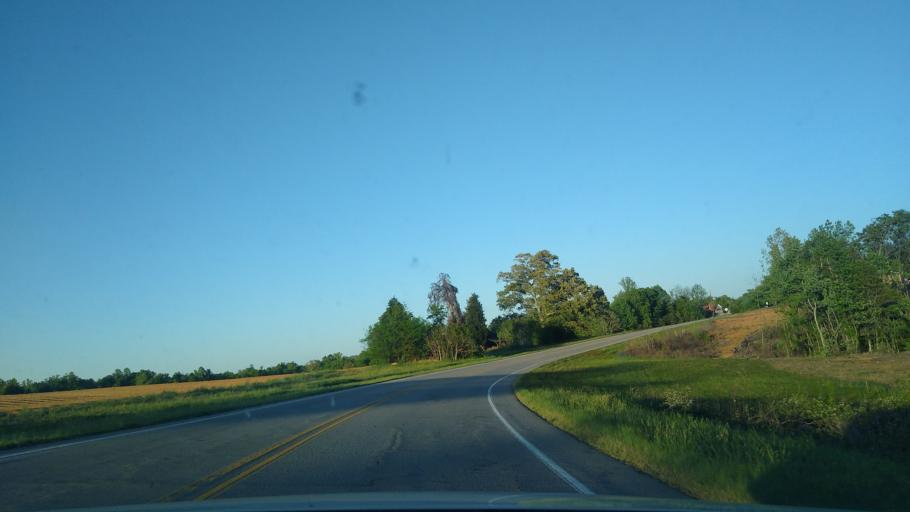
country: US
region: North Carolina
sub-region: Rockingham County
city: Reidsville
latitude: 36.3788
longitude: -79.5910
